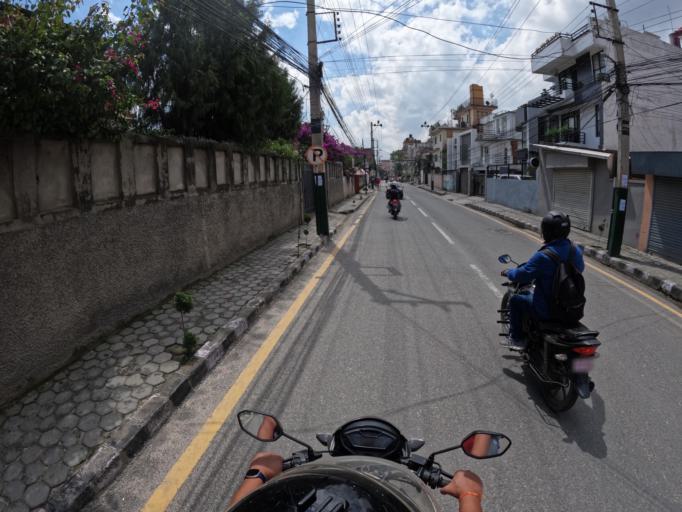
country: NP
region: Central Region
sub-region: Bagmati Zone
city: Patan
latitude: 27.6870
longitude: 85.3118
